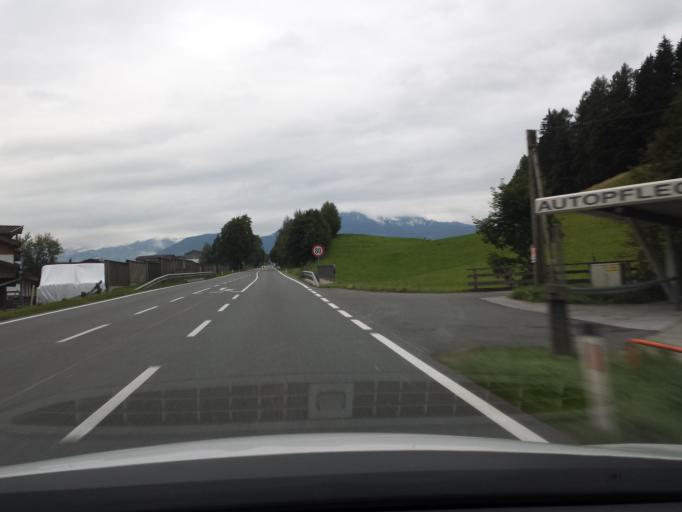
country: AT
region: Salzburg
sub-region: Politischer Bezirk Zell am See
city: Saalfelden am Steinernen Meer
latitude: 47.4511
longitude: 12.8338
